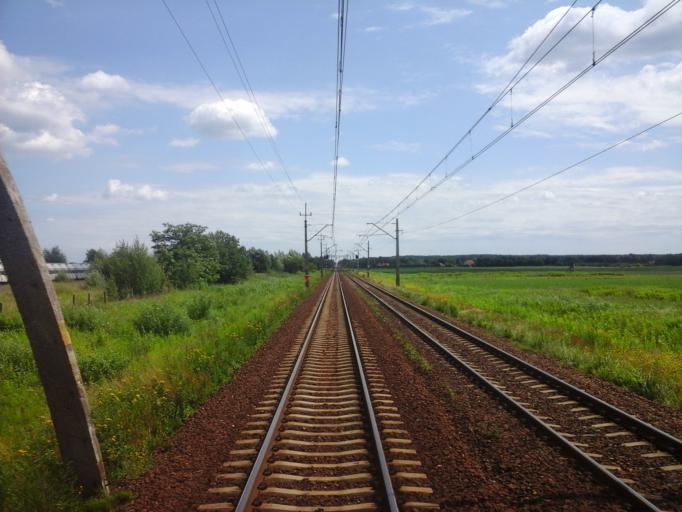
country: PL
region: West Pomeranian Voivodeship
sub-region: Powiat gryfinski
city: Stare Czarnowo
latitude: 53.3874
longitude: 14.7244
